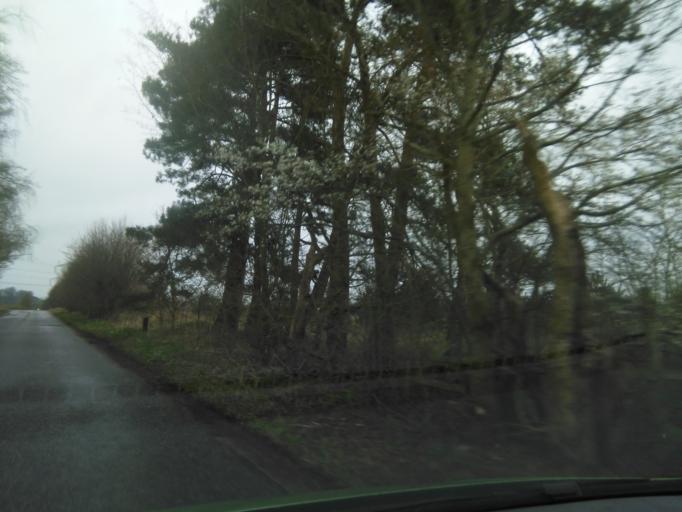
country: DK
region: Central Jutland
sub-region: Arhus Kommune
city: Kolt
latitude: 56.1403
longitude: 10.0511
